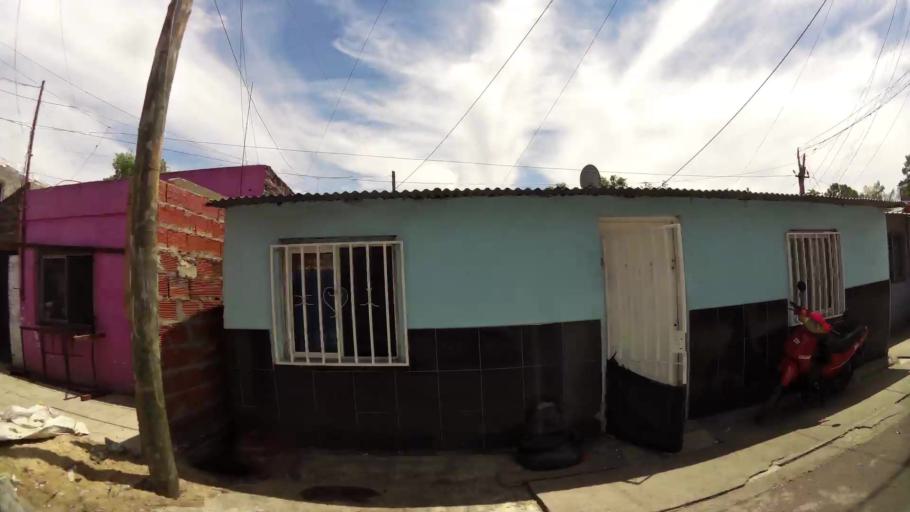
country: AR
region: Santa Fe
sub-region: Departamento de Rosario
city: Rosario
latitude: -32.9844
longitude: -60.6265
